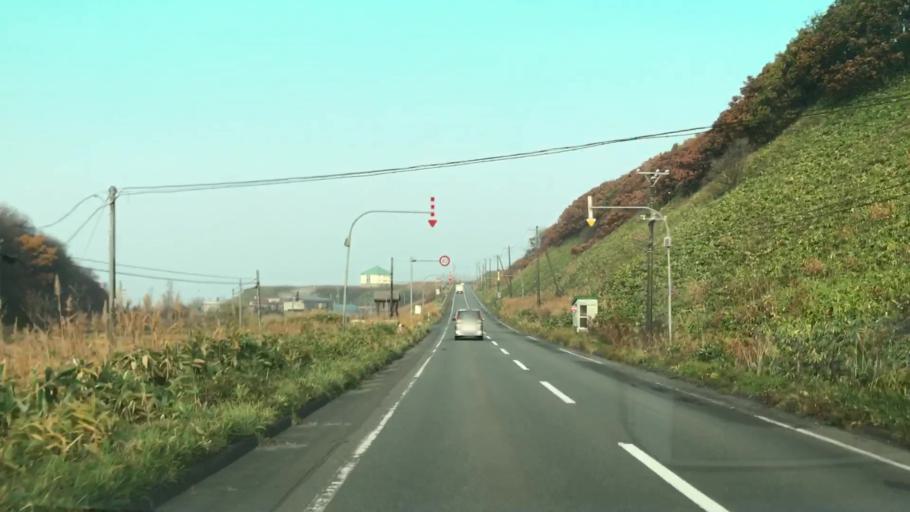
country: JP
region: Hokkaido
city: Ishikari
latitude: 43.3354
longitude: 141.4283
